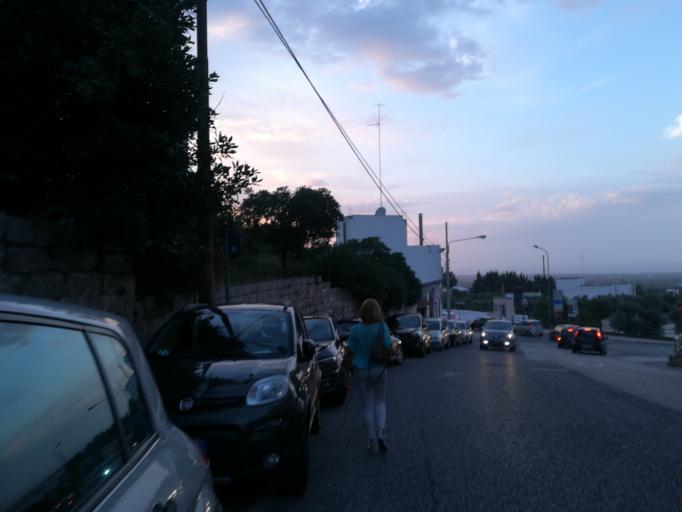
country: IT
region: Apulia
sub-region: Provincia di Brindisi
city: Ostuni
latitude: 40.7313
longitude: 17.5705
